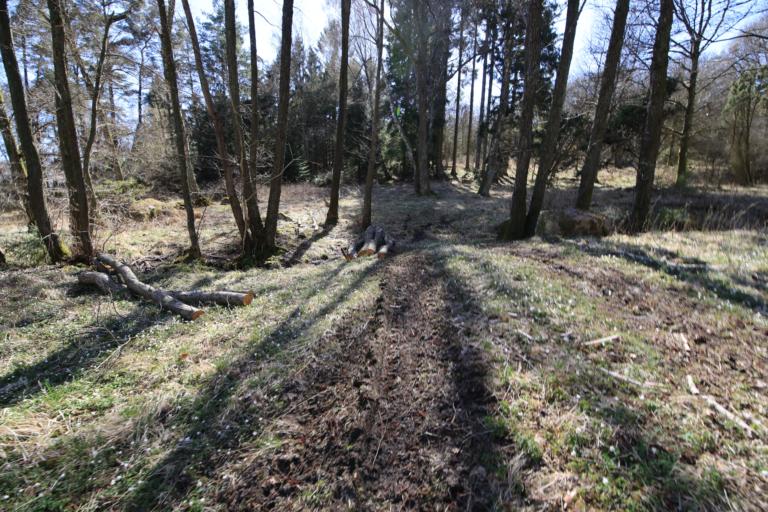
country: SE
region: Halland
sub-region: Varbergs Kommun
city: Varberg
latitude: 57.1675
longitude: 12.2725
